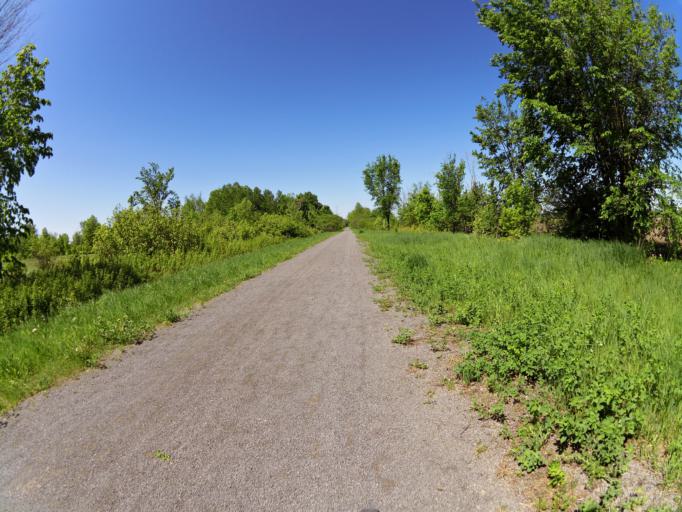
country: CA
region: Ontario
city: Clarence-Rockland
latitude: 45.4219
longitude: -75.3534
